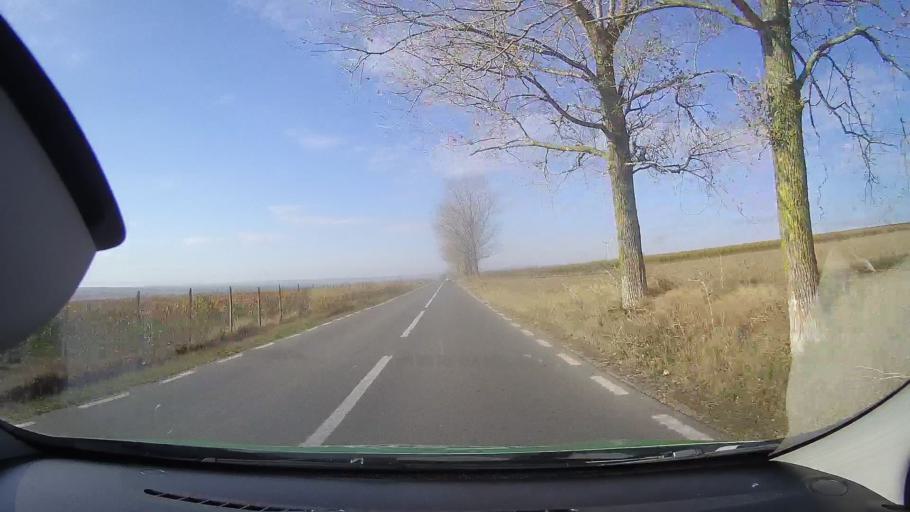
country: RO
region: Tulcea
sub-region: Comuna Valea Nucarilor
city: Iazurile
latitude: 45.0250
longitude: 28.9833
